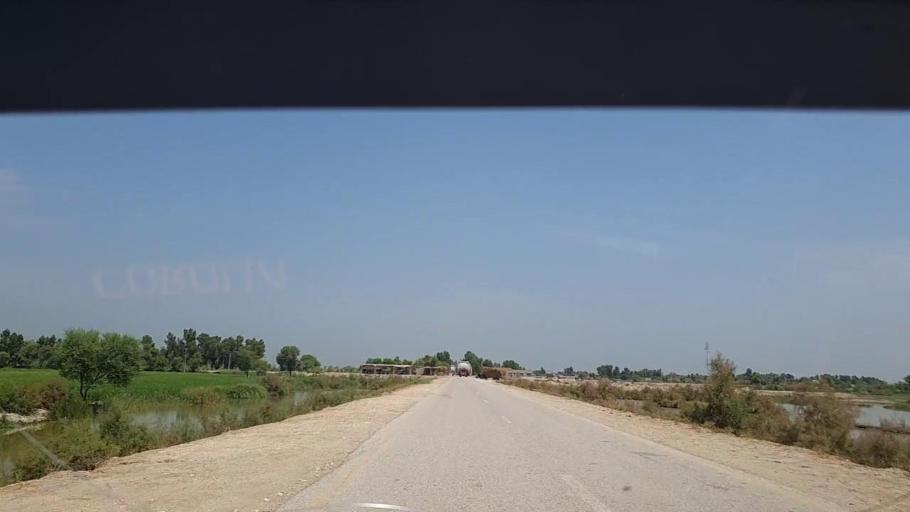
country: PK
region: Sindh
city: Thul
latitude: 28.1146
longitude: 68.8103
